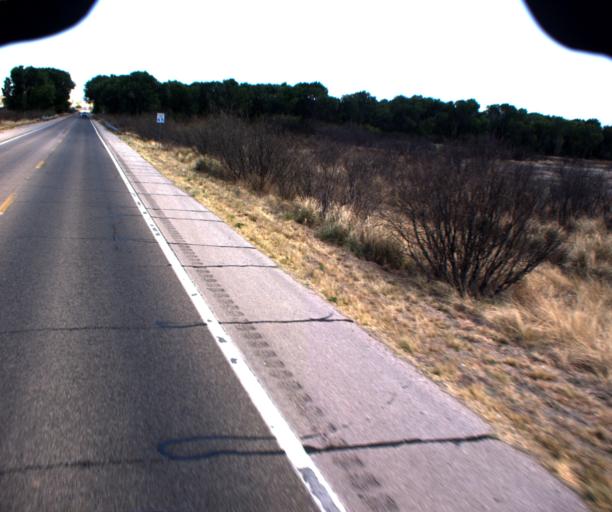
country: US
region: Arizona
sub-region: Cochise County
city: Sierra Vista Southeast
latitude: 31.3799
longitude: -110.1135
